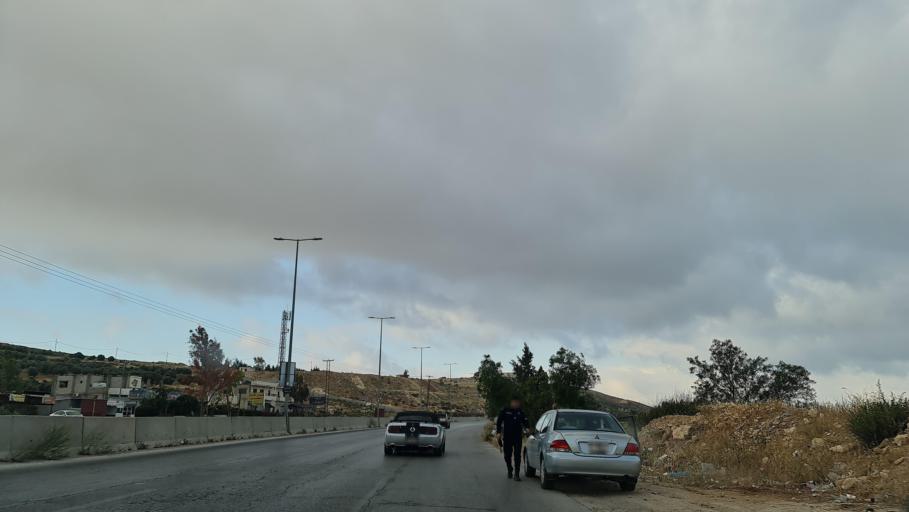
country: JO
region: Amman
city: Al Jubayhah
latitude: 32.0890
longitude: 35.8940
